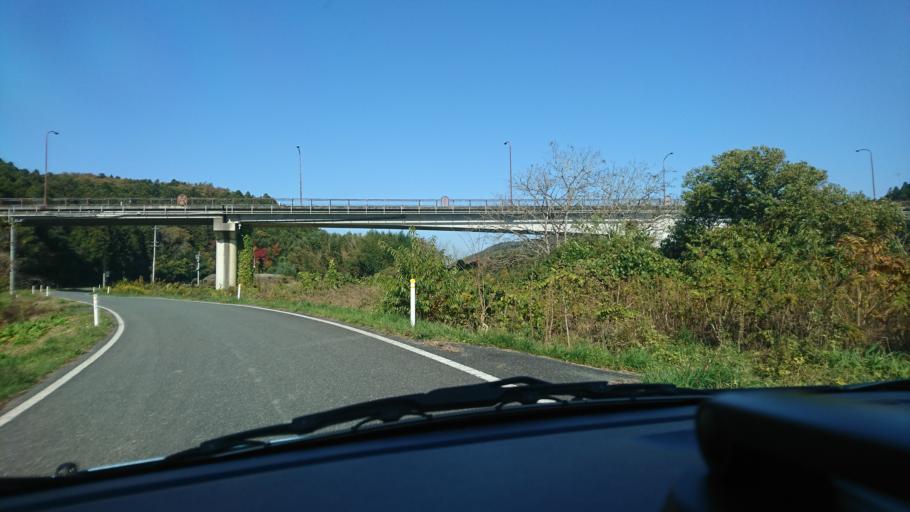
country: JP
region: Iwate
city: Ichinoseki
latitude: 38.7942
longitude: 141.2459
